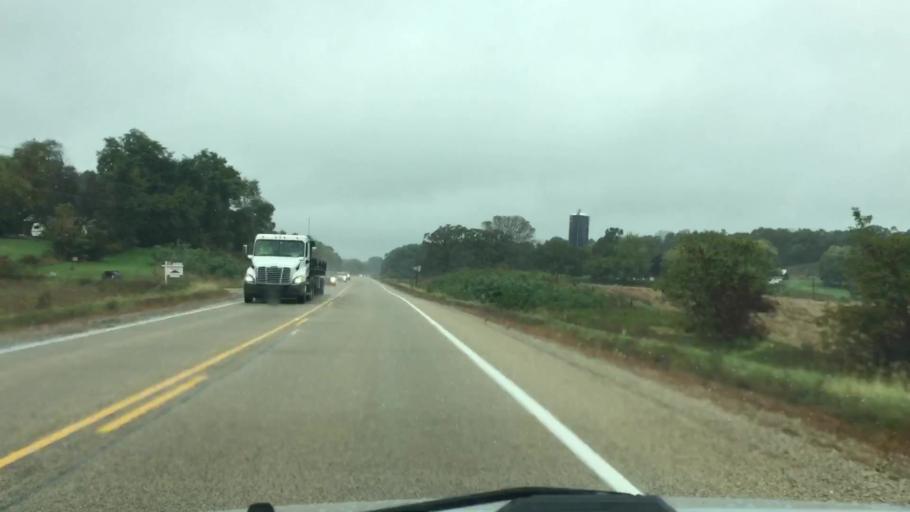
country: US
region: Wisconsin
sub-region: Jefferson County
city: Palmyra
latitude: 42.8850
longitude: -88.5667
